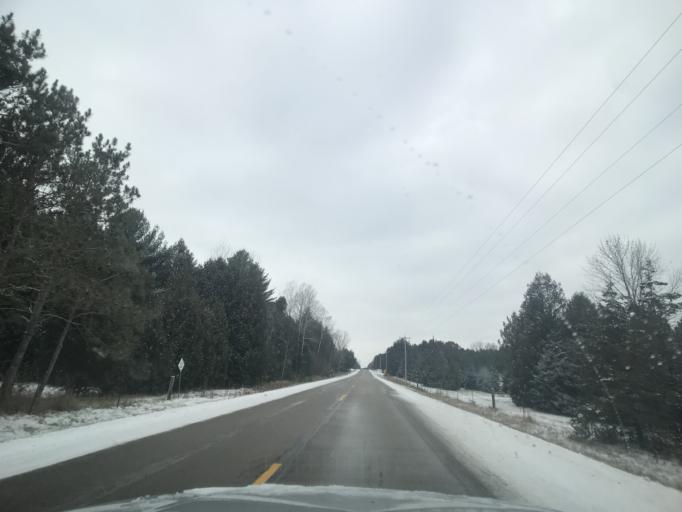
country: US
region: Wisconsin
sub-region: Brown County
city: Suamico
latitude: 44.7062
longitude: -88.0881
